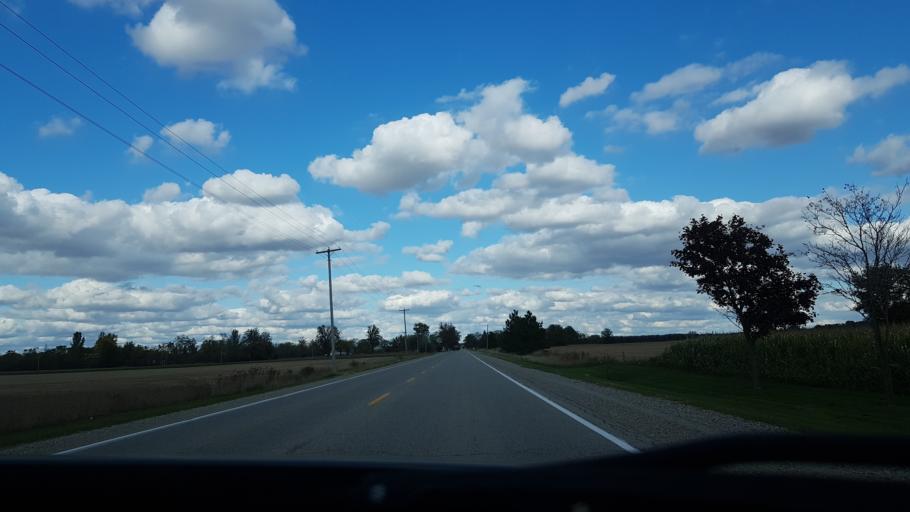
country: CA
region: Ontario
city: South Huron
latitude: 43.0942
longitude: -81.5720
